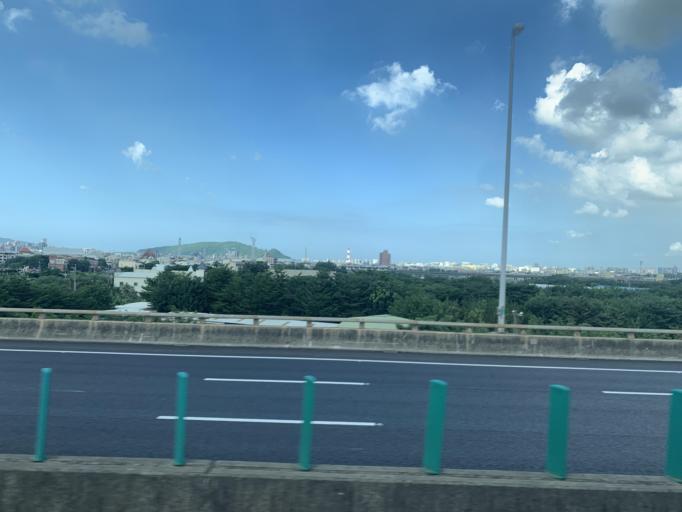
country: TW
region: Taiwan
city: Fengshan
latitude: 22.7047
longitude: 120.3602
